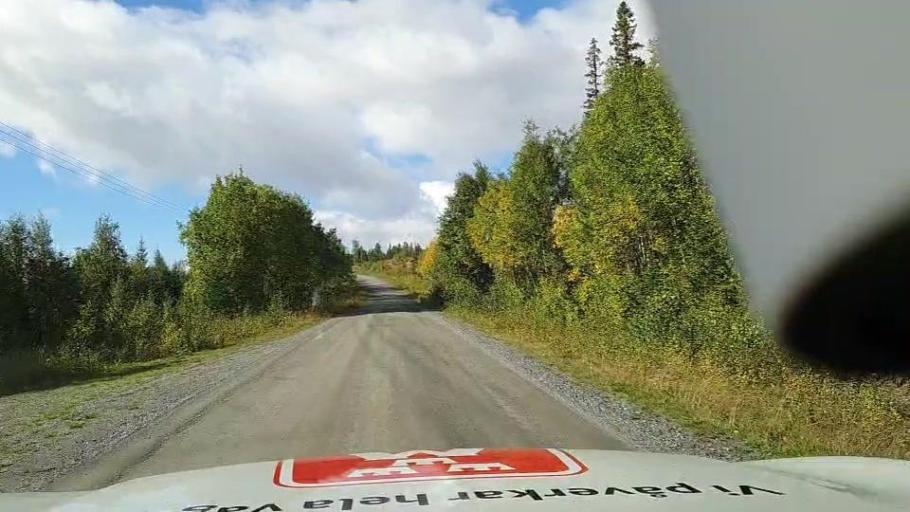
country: SE
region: Jaemtland
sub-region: Are Kommun
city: Jarpen
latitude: 63.1912
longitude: 13.6431
